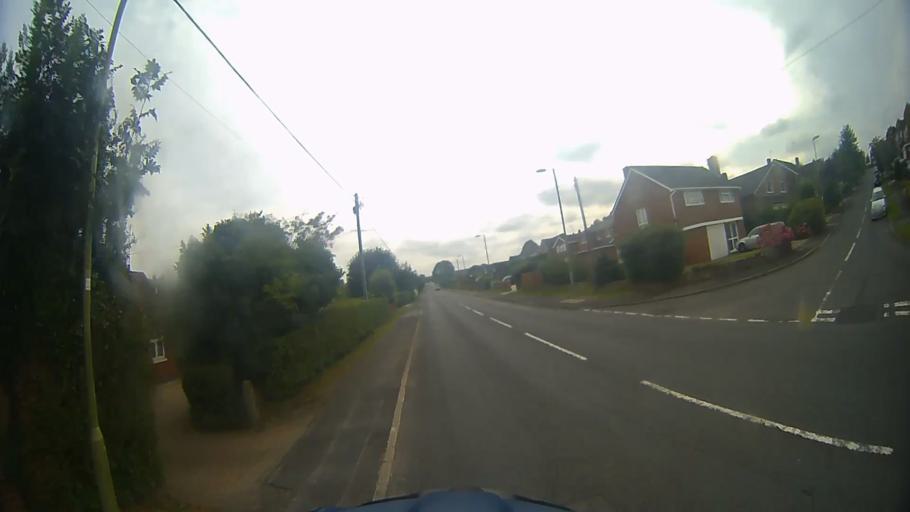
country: GB
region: England
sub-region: Hampshire
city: Basingstoke
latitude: 51.2511
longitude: -1.1387
